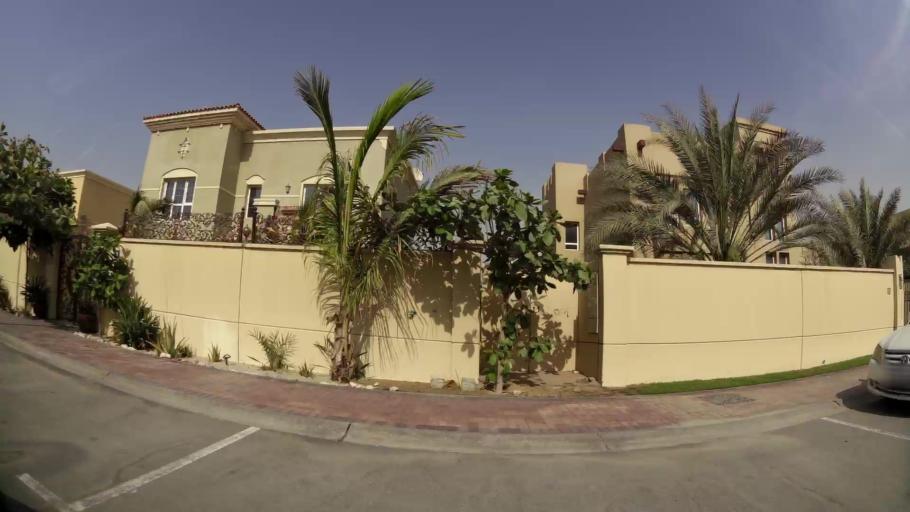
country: AE
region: Ash Shariqah
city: Sharjah
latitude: 25.2661
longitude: 55.4539
